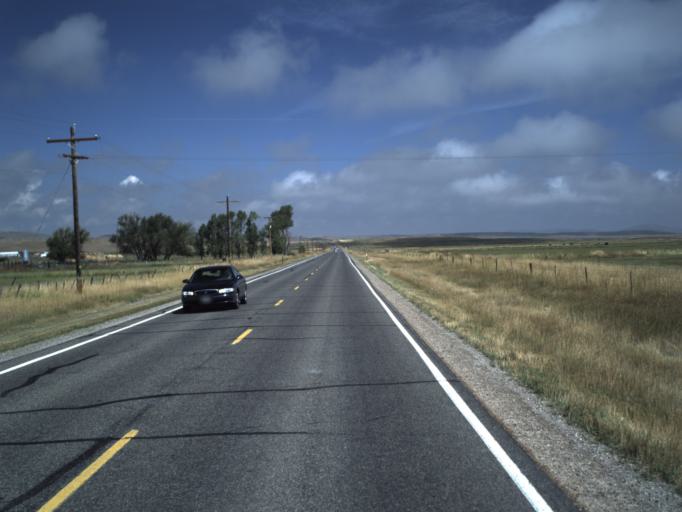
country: US
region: Utah
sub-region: Rich County
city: Randolph
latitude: 41.7147
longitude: -111.1594
